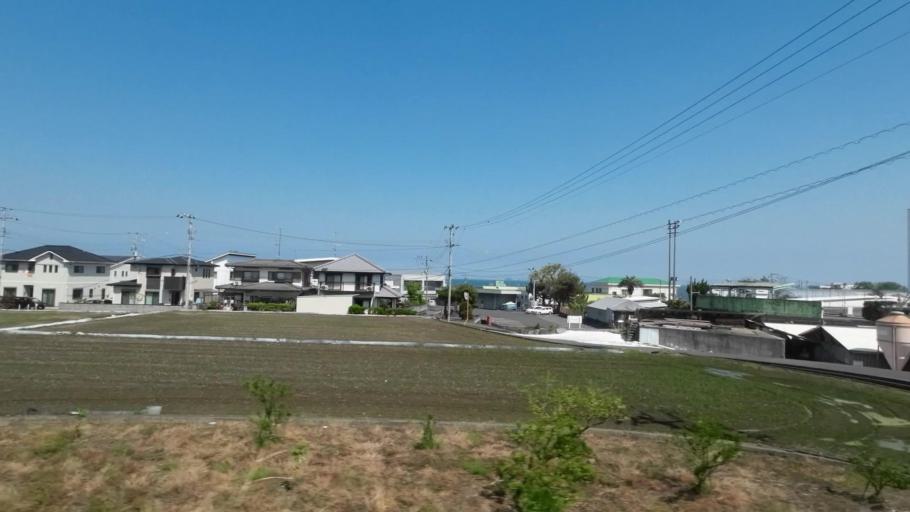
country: JP
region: Ehime
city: Kawanoecho
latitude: 33.9729
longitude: 133.5238
